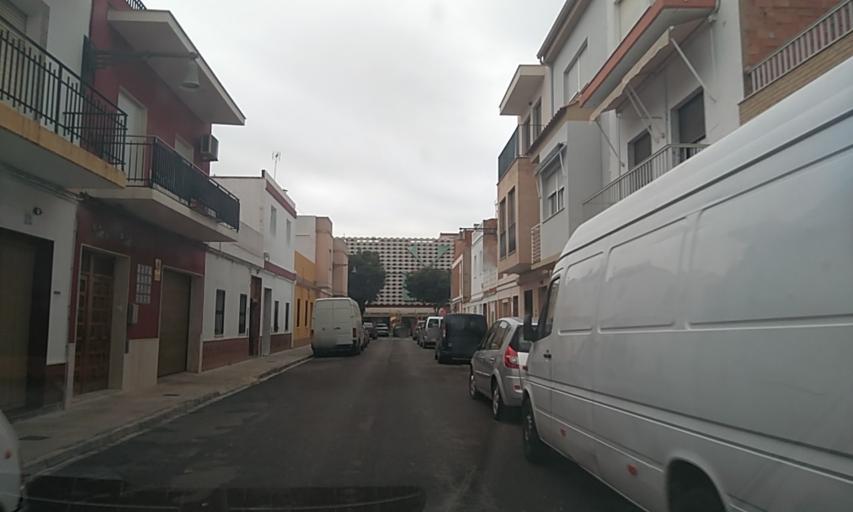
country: ES
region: Valencia
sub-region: Provincia de Valencia
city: L'Alcudia
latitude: 39.1916
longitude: -0.5061
